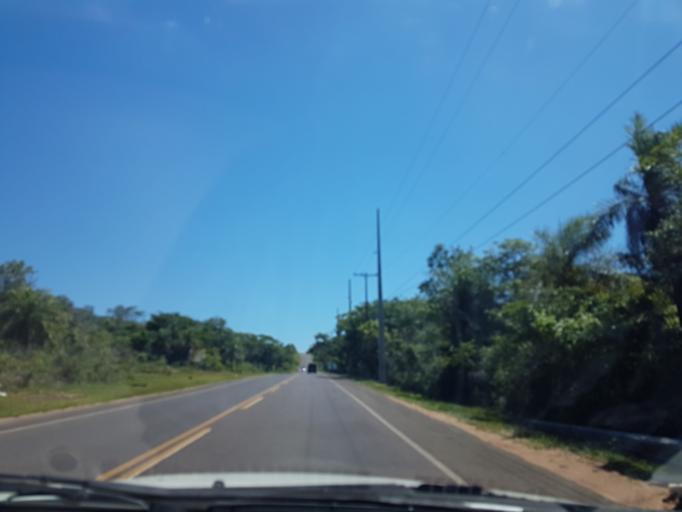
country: PY
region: Cordillera
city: Altos
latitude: -25.2503
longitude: -57.2383
